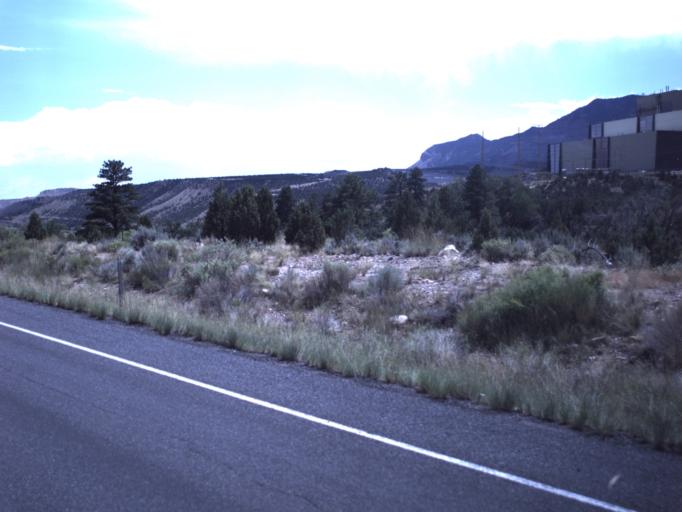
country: US
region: Utah
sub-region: Emery County
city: Huntington
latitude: 39.3857
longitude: -111.0781
